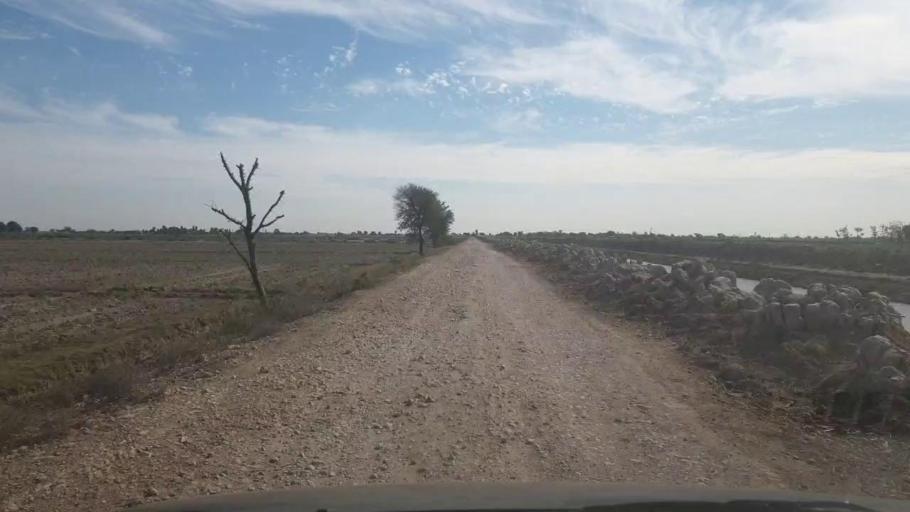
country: PK
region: Sindh
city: Mirwah Gorchani
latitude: 25.4278
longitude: 69.2003
